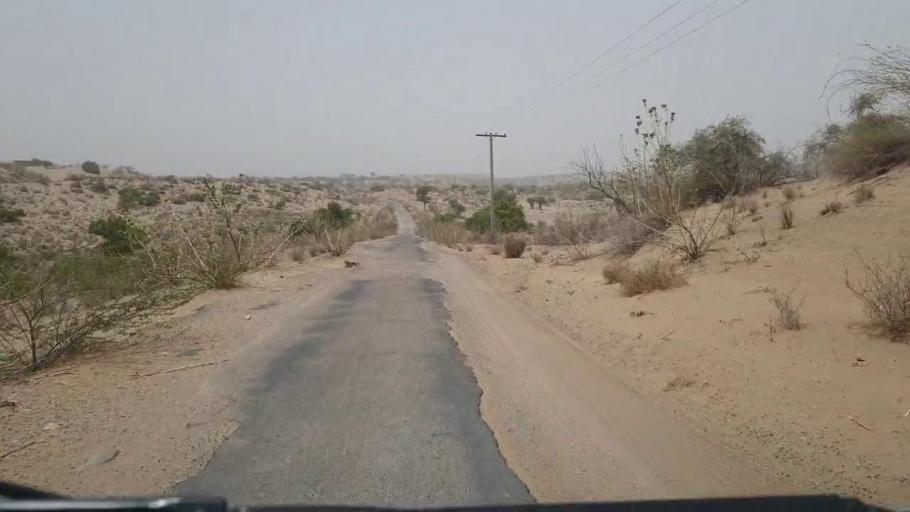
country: PK
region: Sindh
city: Naukot
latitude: 24.7526
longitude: 69.5519
